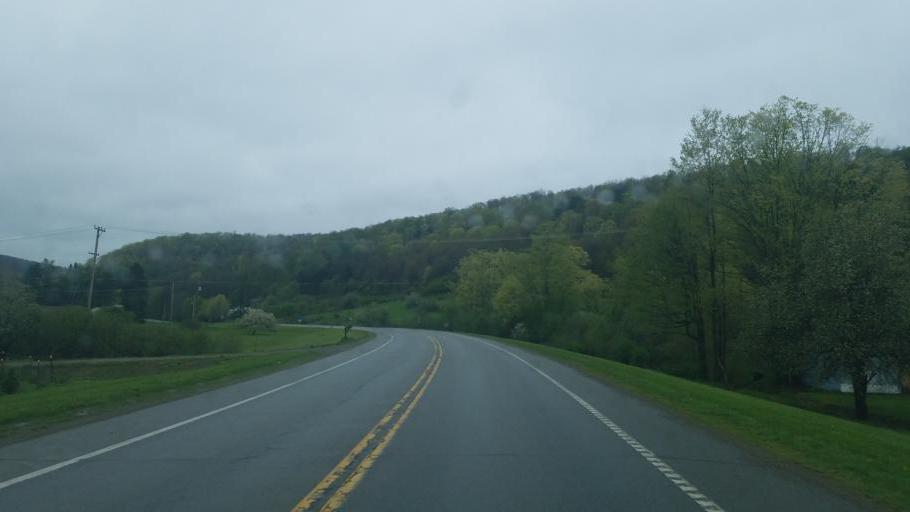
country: US
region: Pennsylvania
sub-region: Potter County
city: Coudersport
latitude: 41.8100
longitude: -78.0172
